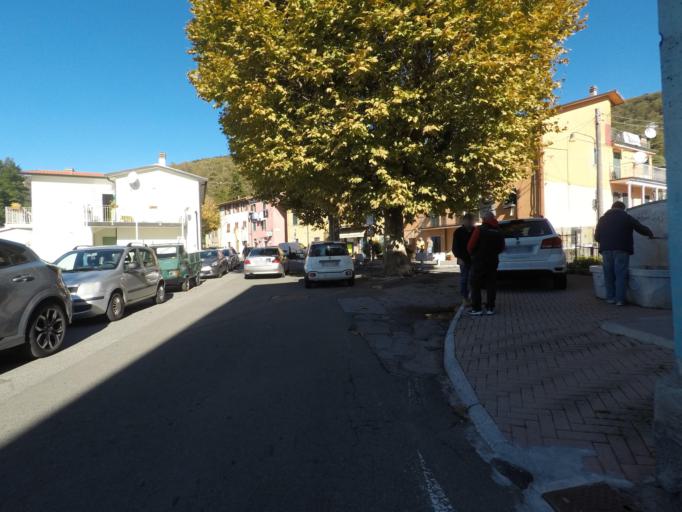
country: IT
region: Liguria
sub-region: Provincia di La Spezia
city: Casano-Dogana-Isola
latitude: 44.1130
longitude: 10.0739
